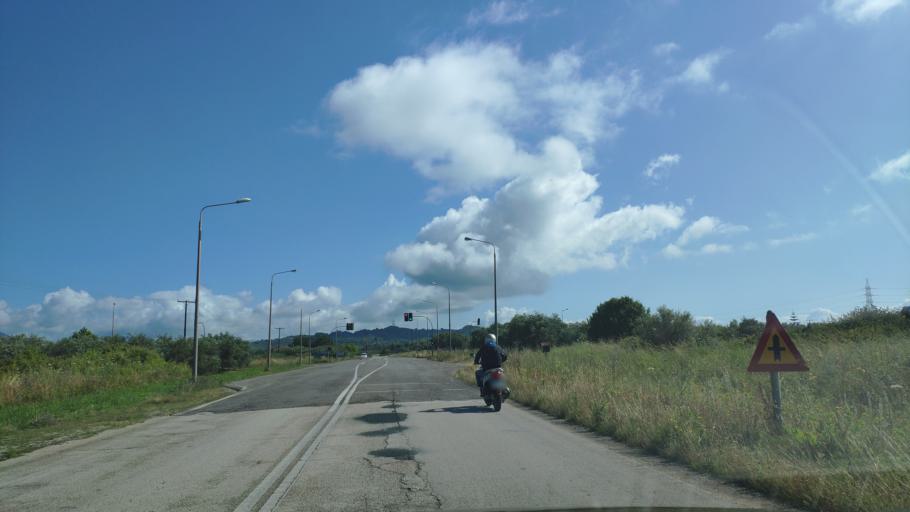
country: GR
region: Epirus
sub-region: Nomos Prevezis
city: Preveza
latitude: 39.0014
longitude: 20.7168
